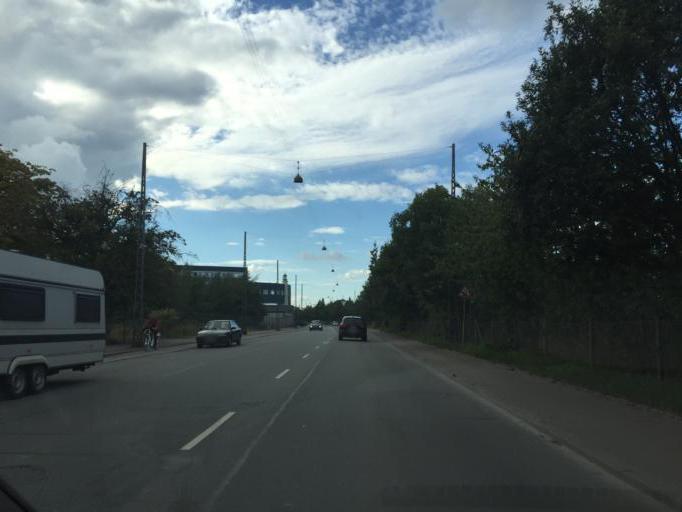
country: DK
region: Capital Region
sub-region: Kobenhavn
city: Christianshavn
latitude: 55.6694
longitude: 12.6140
